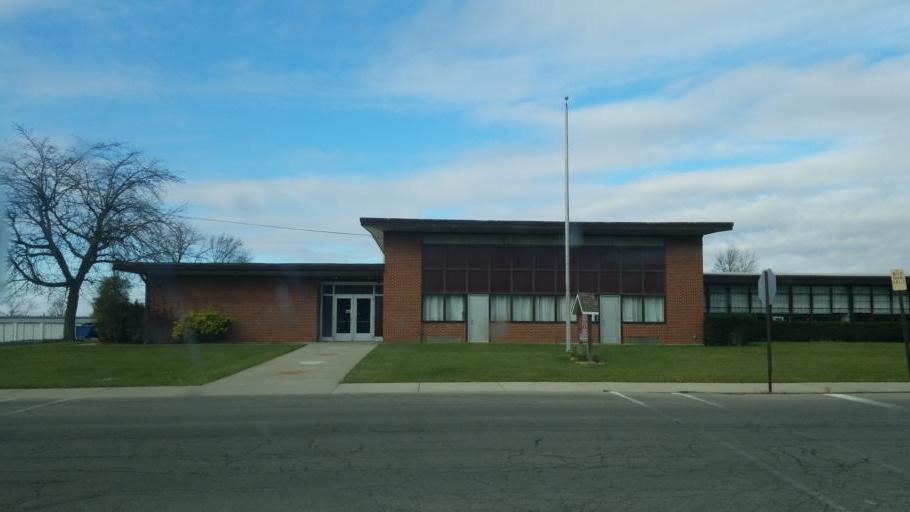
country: US
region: Ohio
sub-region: Hardin County
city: Kenton
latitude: 40.6528
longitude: -83.6210
